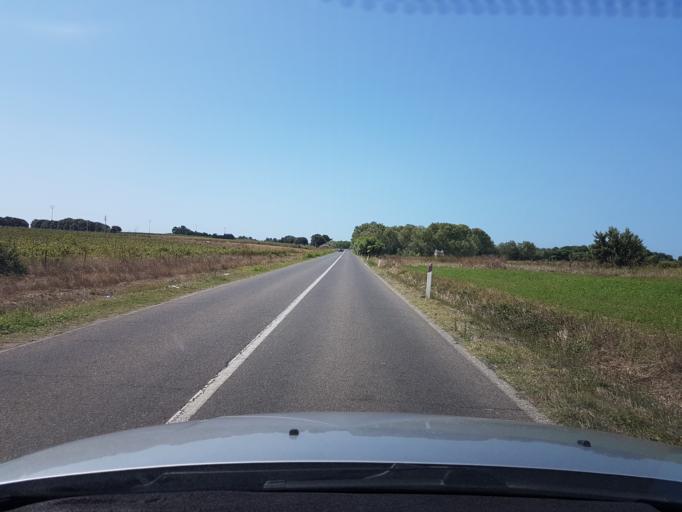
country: IT
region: Sardinia
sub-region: Provincia di Oristano
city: Riola Sardo
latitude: 40.0211
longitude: 8.4821
